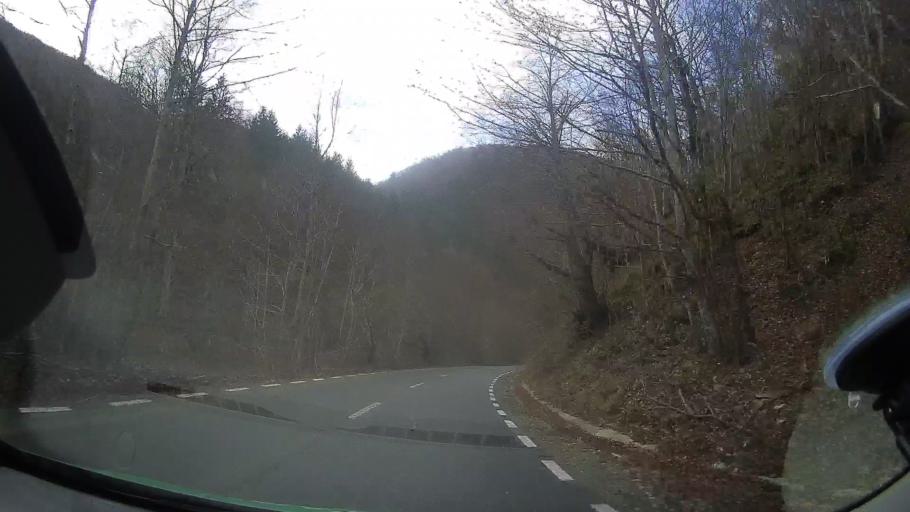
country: RO
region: Cluj
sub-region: Comuna Valea Ierii
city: Valea Ierii
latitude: 46.6296
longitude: 23.3803
